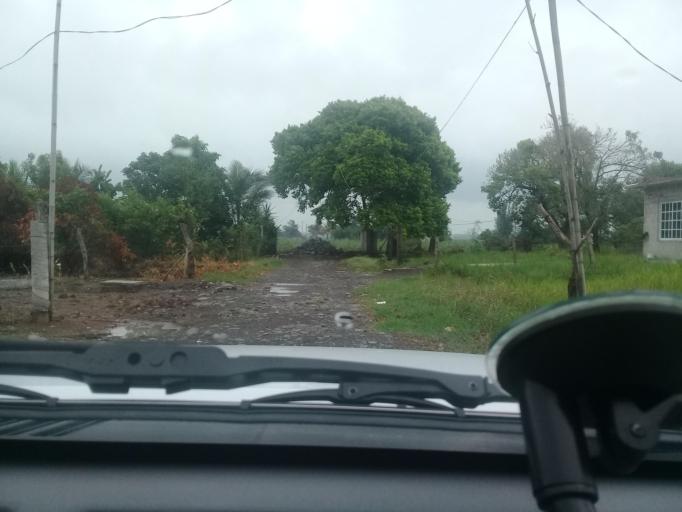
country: MX
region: Veracruz
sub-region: La Antigua
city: Nicolas Blanco (San Pancho)
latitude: 19.3391
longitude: -96.3606
